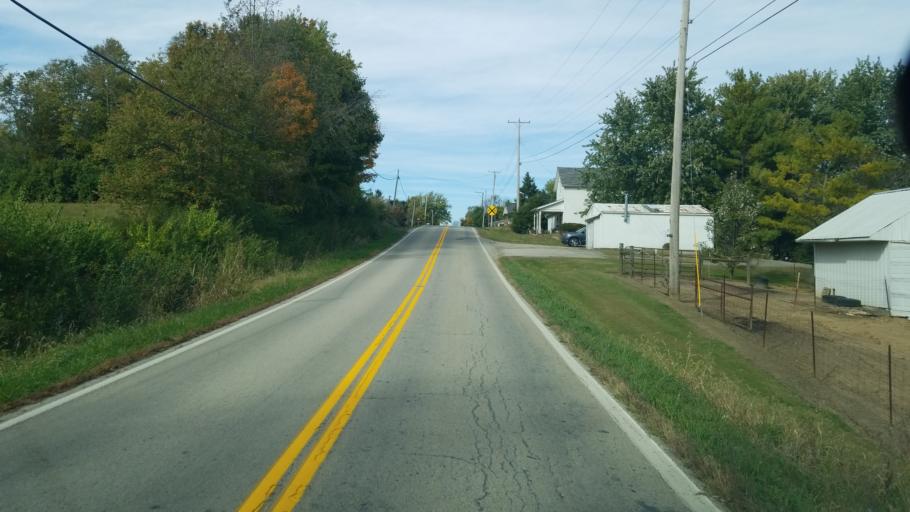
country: US
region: Ohio
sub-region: Highland County
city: Leesburg
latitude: 39.3333
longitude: -83.5923
